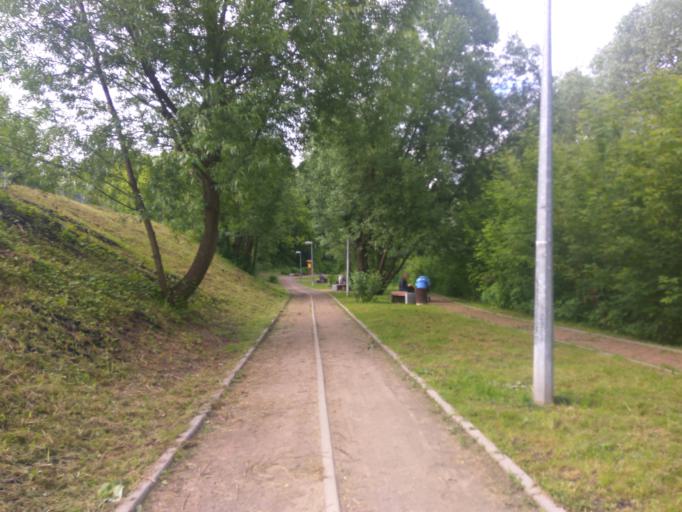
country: RU
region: Moscow
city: Vorob'yovo
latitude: 55.7271
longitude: 37.5185
